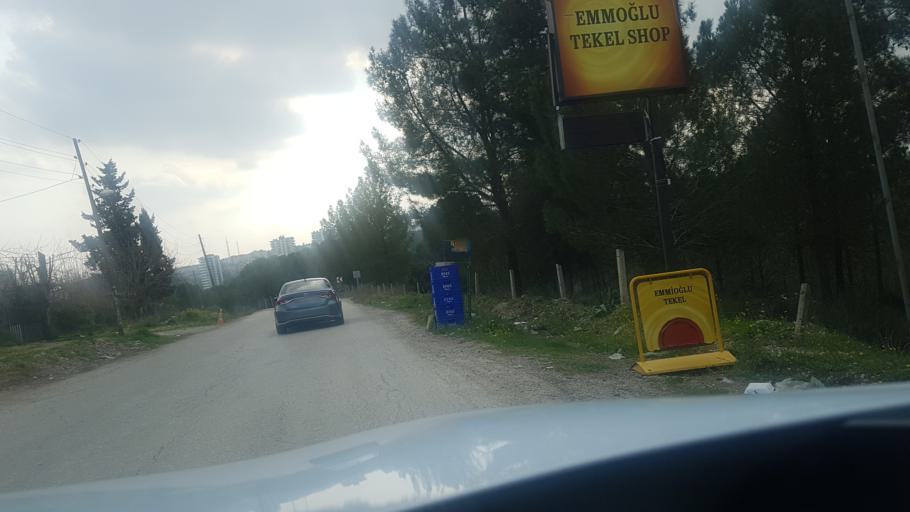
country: TR
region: Adana
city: Seyhan
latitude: 37.0589
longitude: 35.2561
